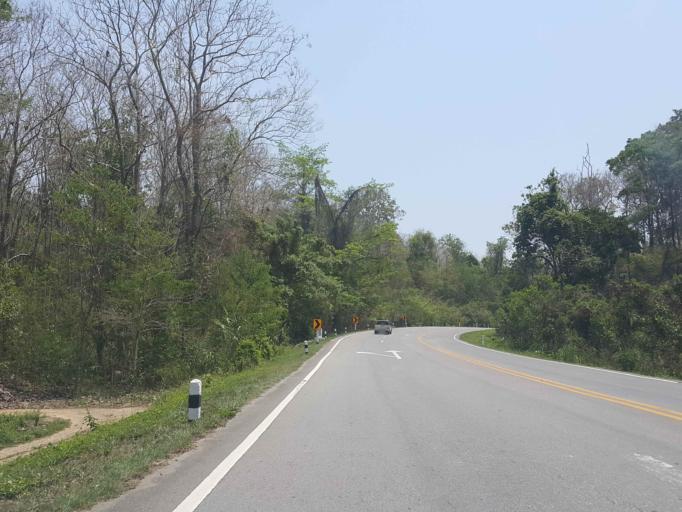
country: TH
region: Chiang Mai
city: Mae On
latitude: 18.9341
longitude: 99.2385
